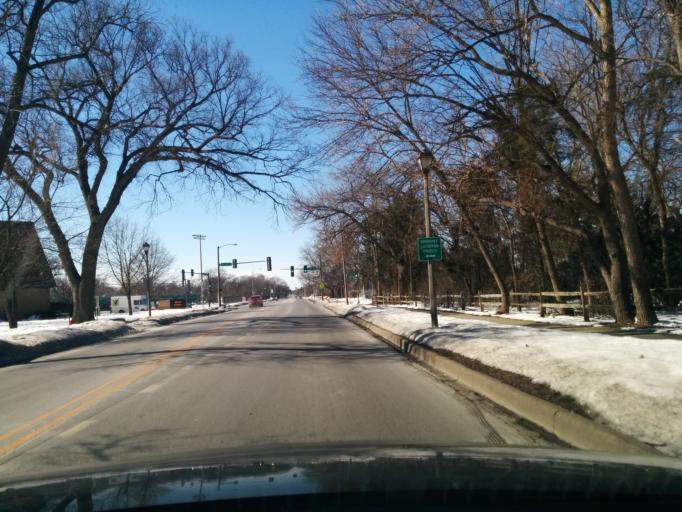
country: US
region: Illinois
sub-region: DuPage County
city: Elmhurst
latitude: 41.8904
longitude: -87.9484
